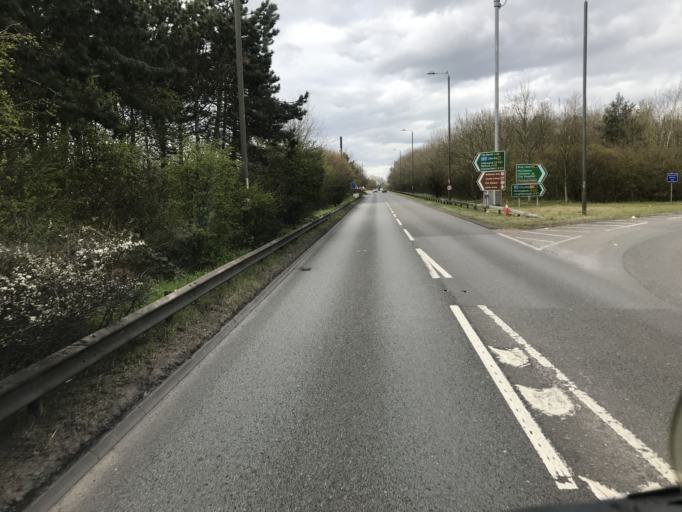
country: GB
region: England
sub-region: Derby
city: Derby
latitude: 52.9217
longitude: -1.5140
